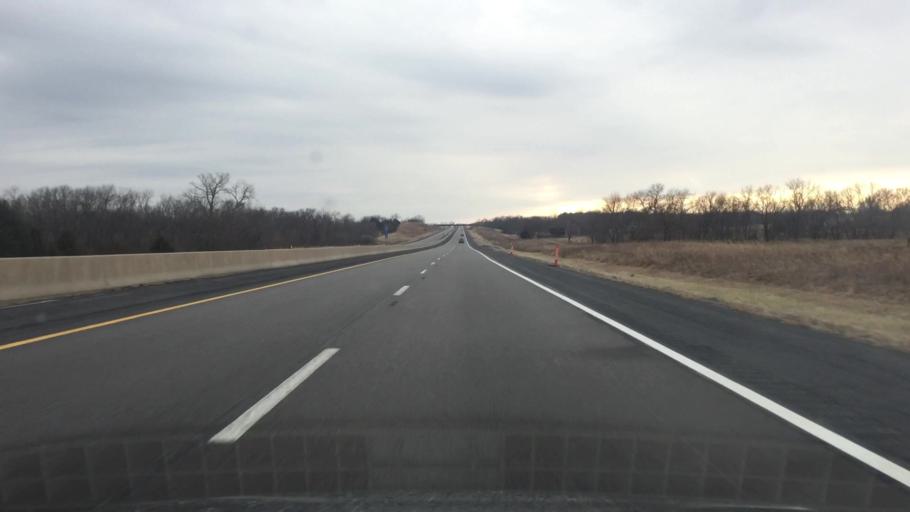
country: US
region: Kansas
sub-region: Osage County
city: Osage City
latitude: 38.7340
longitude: -95.9574
